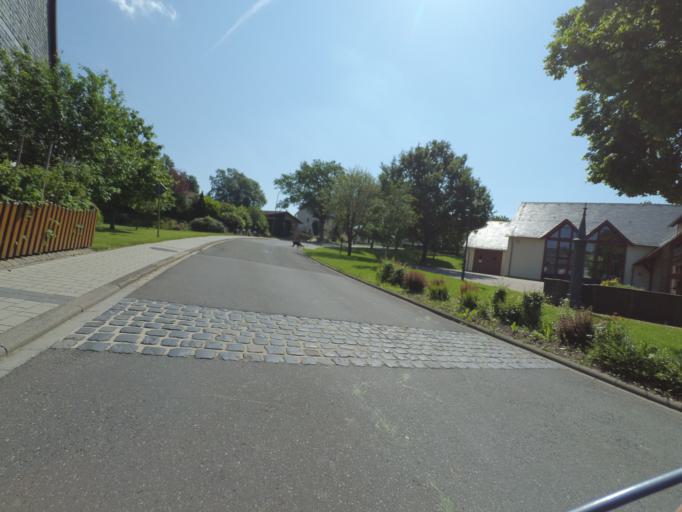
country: DE
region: Rheinland-Pfalz
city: Bell
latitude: 50.0608
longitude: 7.4156
